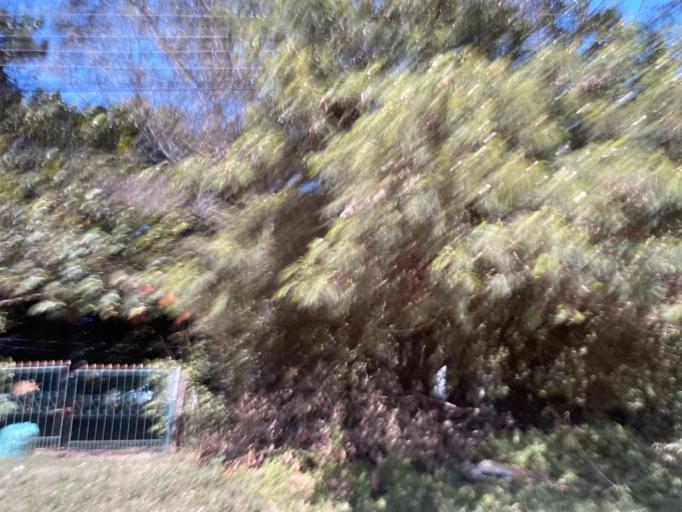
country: PY
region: Misiones
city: San Juan Bautista
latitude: -26.6634
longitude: -57.1456
